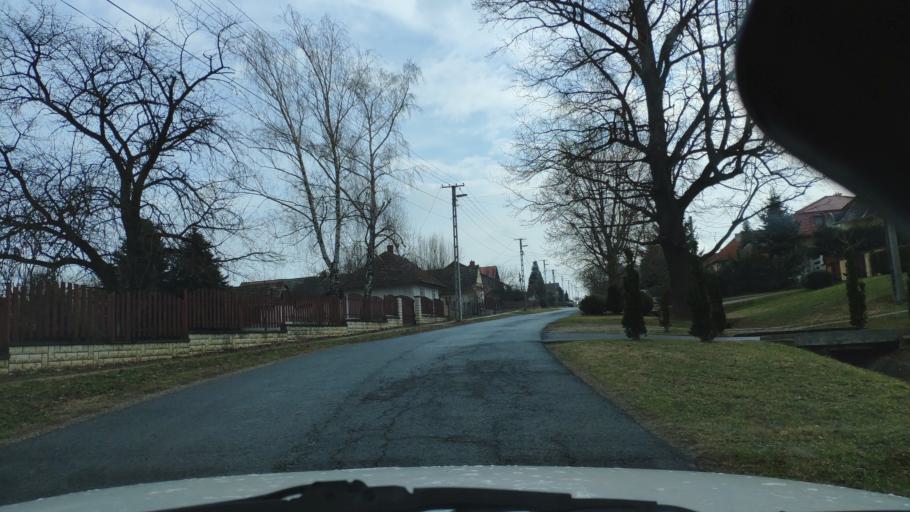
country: HU
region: Zala
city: Nagykanizsa
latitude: 46.4113
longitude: 16.9990
